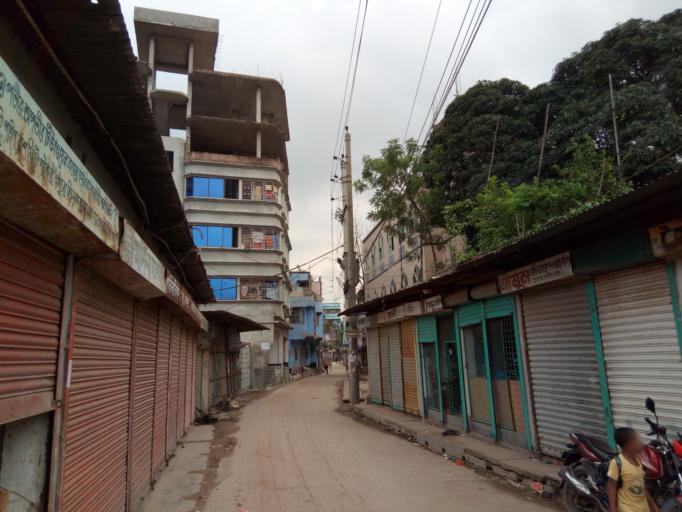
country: BD
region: Dhaka
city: Paltan
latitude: 23.7115
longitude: 90.4921
